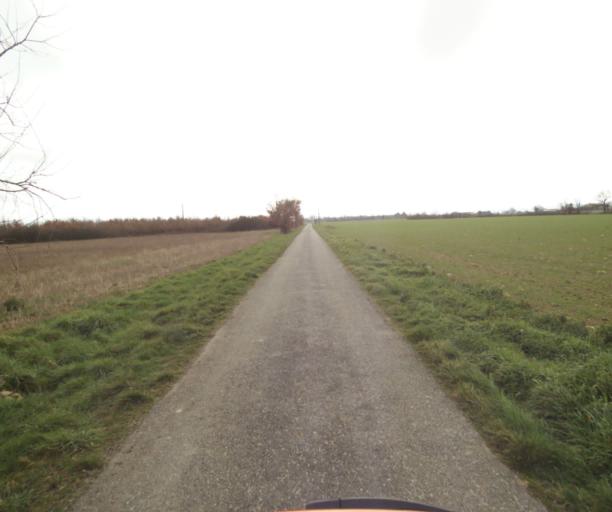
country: FR
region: Languedoc-Roussillon
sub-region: Departement de l'Aude
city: Belpech
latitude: 43.1693
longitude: 1.6862
